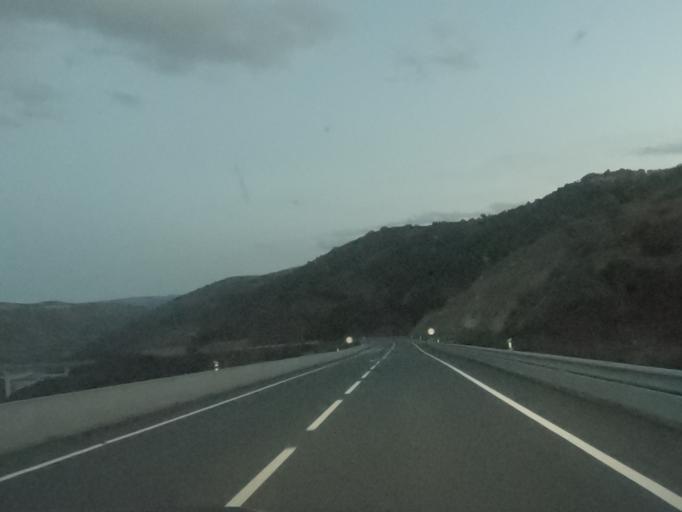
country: PT
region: Braganca
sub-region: Alfandega da Fe
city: Alfandega da Fe
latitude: 41.3144
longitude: -6.9280
